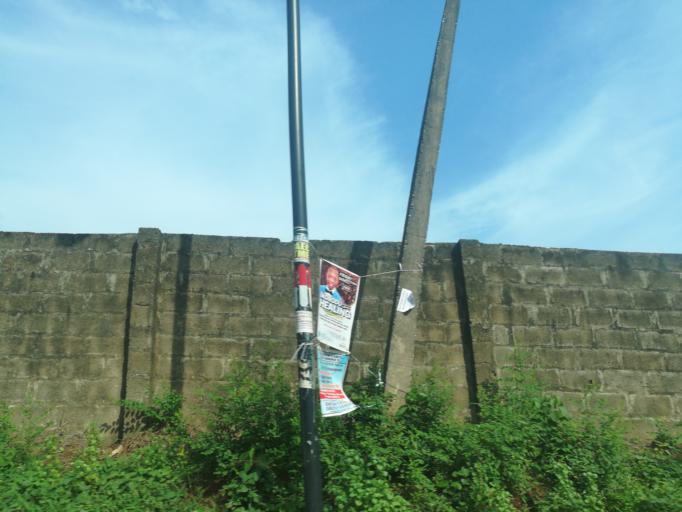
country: NG
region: Lagos
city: Ikorodu
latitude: 6.6306
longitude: 3.5110
